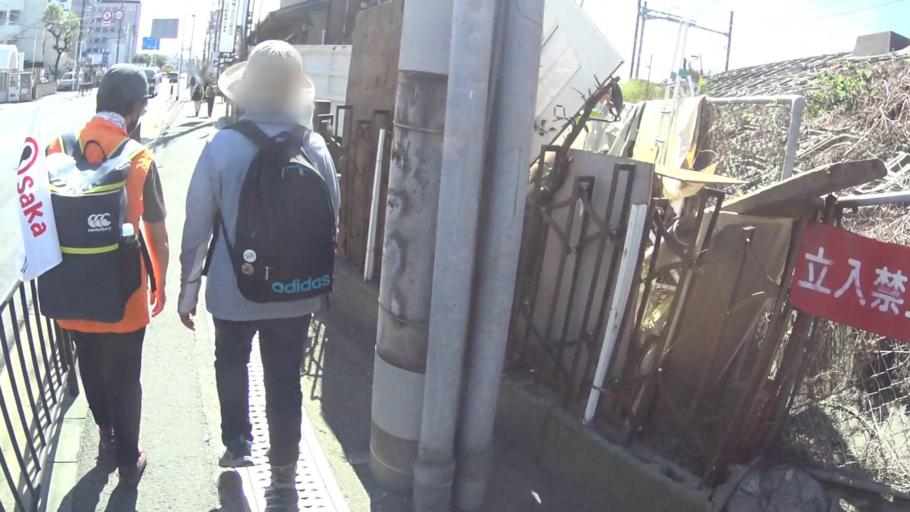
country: JP
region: Ehime
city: Kihoku-cho
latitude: 33.3932
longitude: 132.8503
